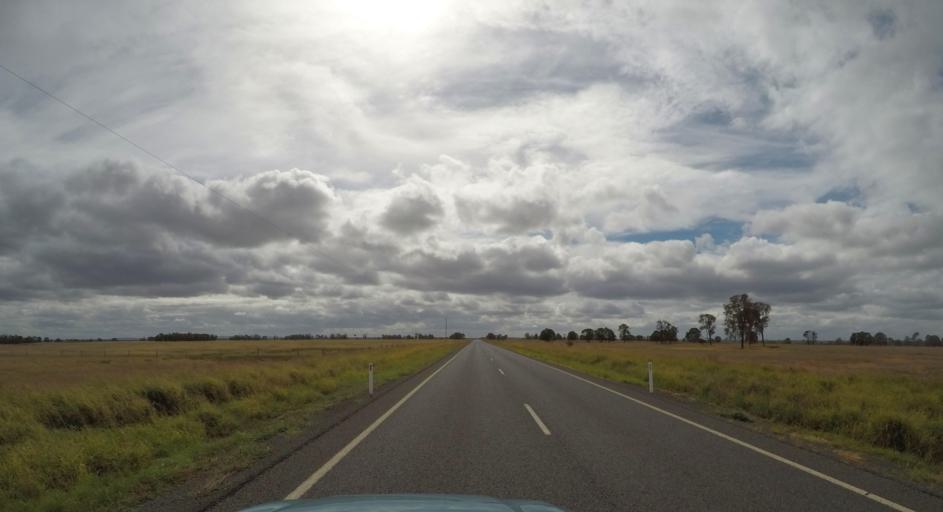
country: AU
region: Queensland
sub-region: South Burnett
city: Kingaroy
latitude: -26.3461
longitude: 151.2514
